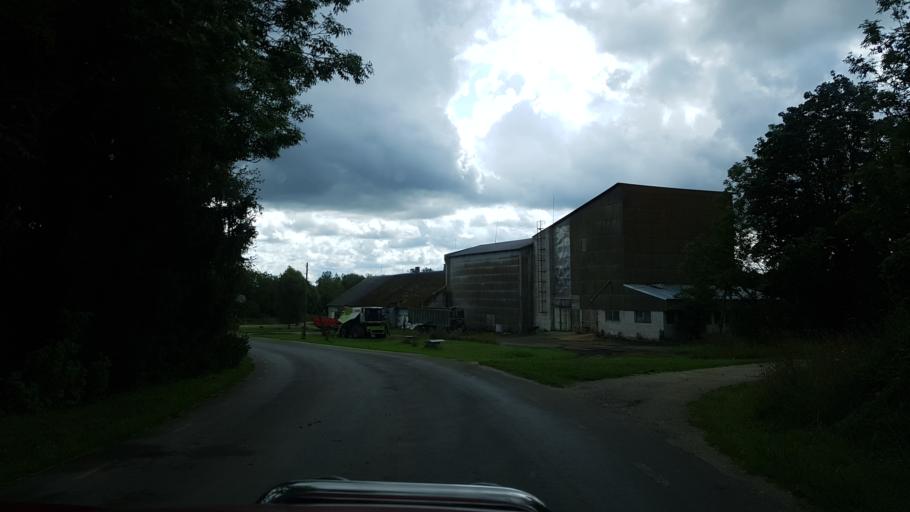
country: EE
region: Laeaene
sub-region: Lihula vald
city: Lihula
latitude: 58.7255
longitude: 23.9532
